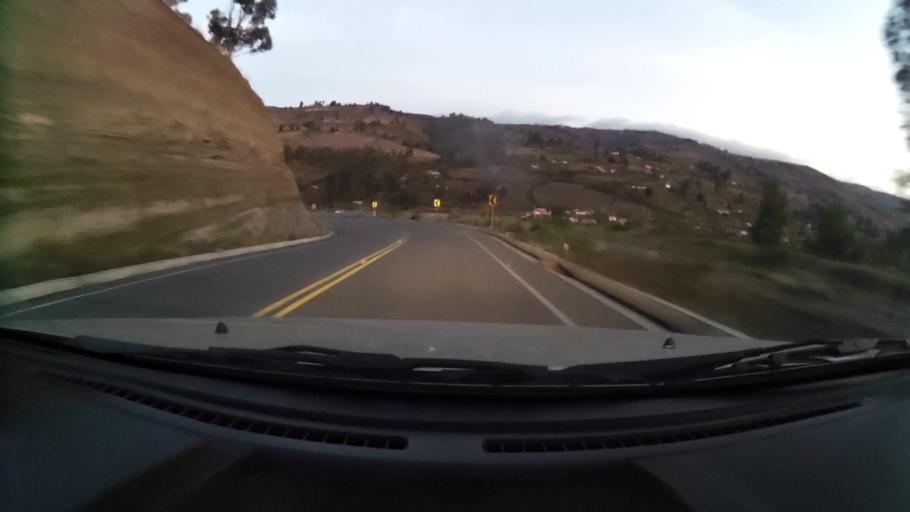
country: EC
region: Chimborazo
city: Riobamba
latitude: -1.9025
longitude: -78.6942
